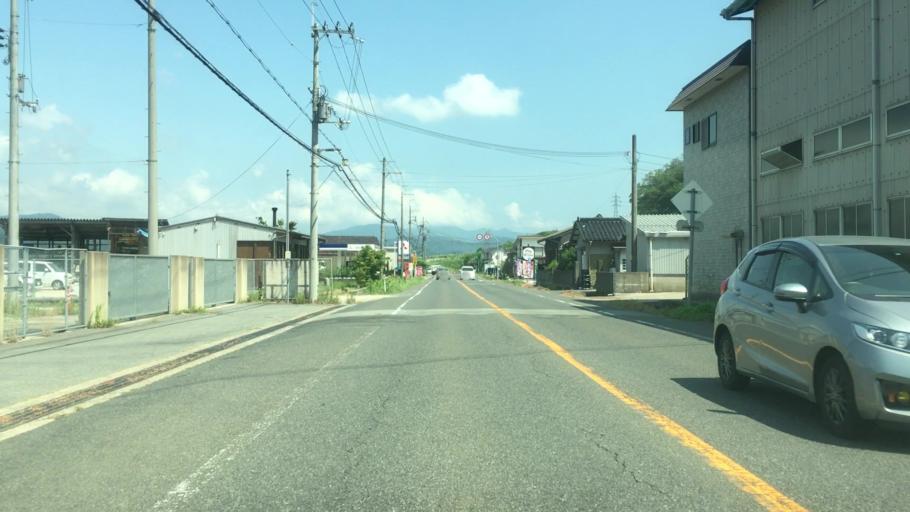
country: JP
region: Hyogo
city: Toyooka
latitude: 35.5652
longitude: 134.7919
